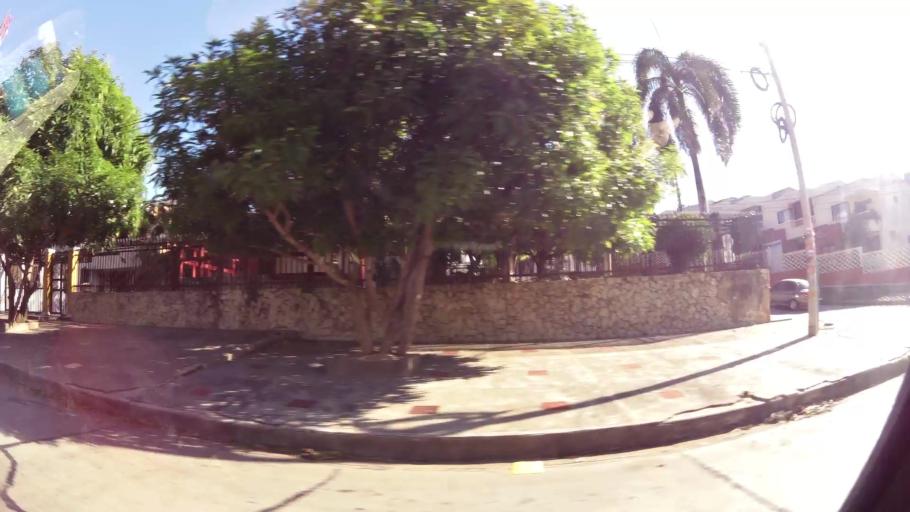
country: CO
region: Atlantico
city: Barranquilla
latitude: 11.0029
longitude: -74.8319
